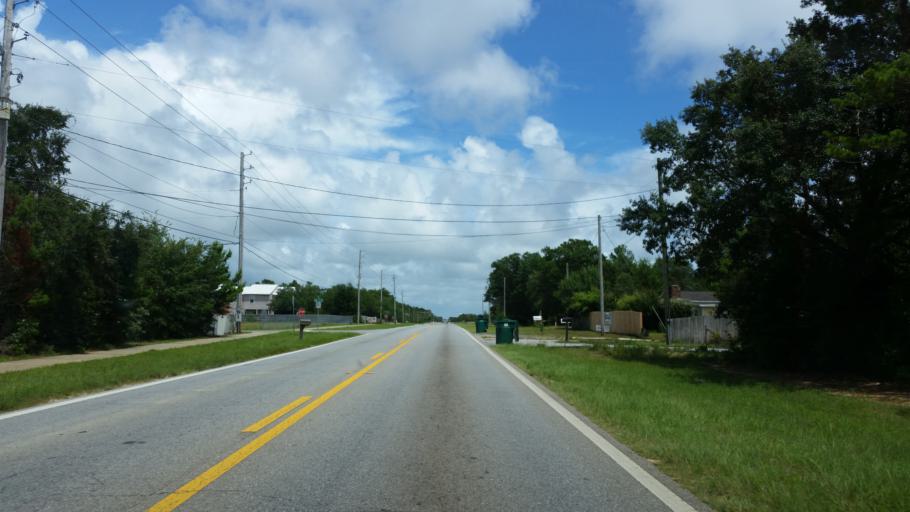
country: US
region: Florida
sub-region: Santa Rosa County
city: Holley
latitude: 30.4328
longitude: -86.9028
